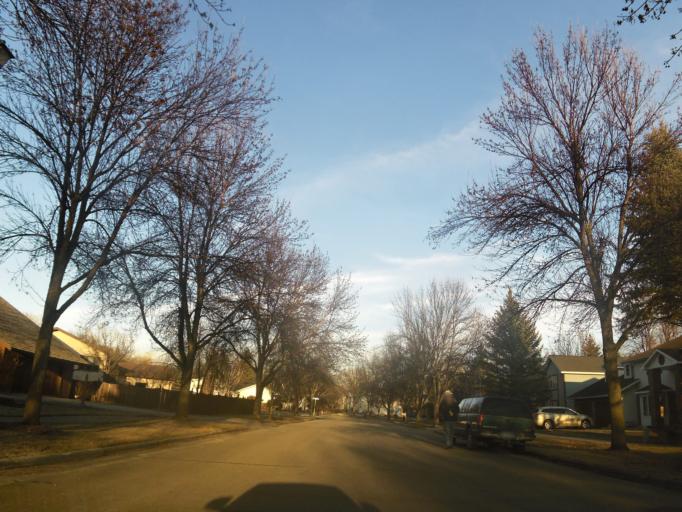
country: US
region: North Dakota
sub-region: Grand Forks County
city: Grand Forks
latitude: 47.8773
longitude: -97.0272
